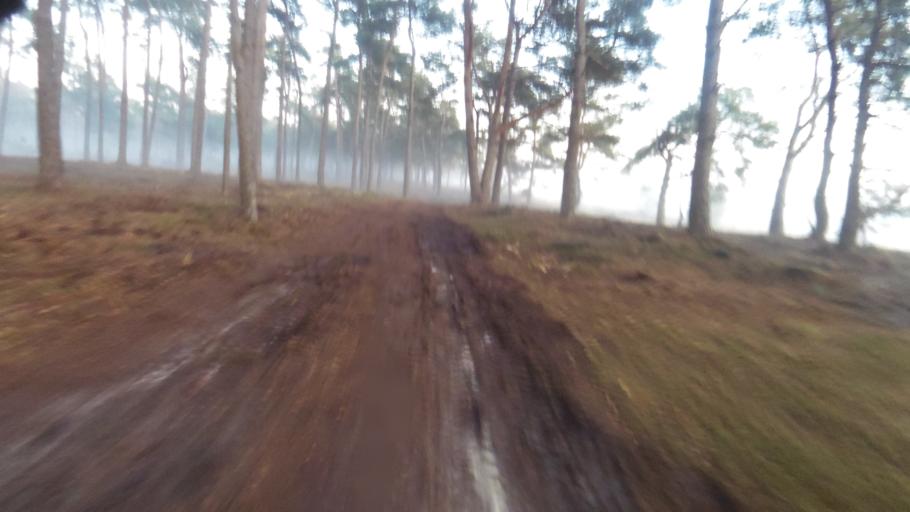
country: NL
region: Gelderland
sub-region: Gemeente Apeldoorn
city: Uddel
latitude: 52.2501
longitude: 5.7947
